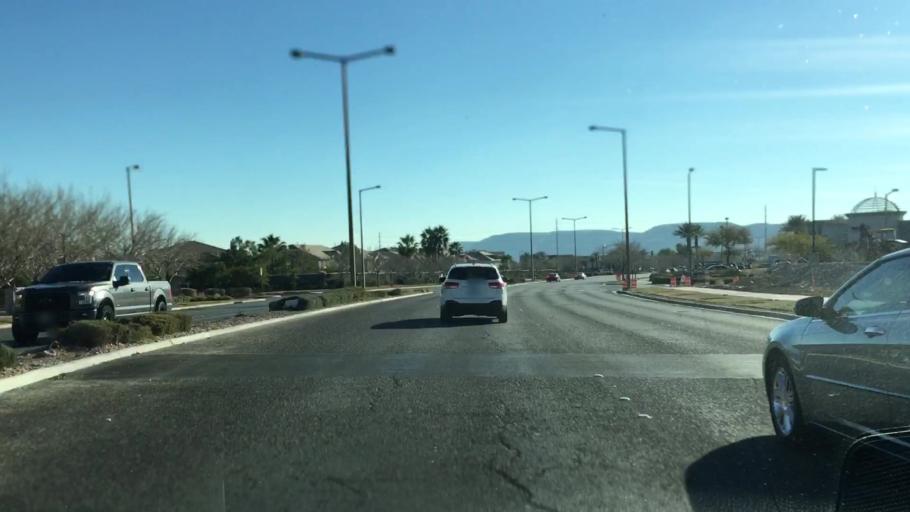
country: US
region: Nevada
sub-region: Clark County
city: Summerlin South
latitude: 36.1262
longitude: -115.3246
